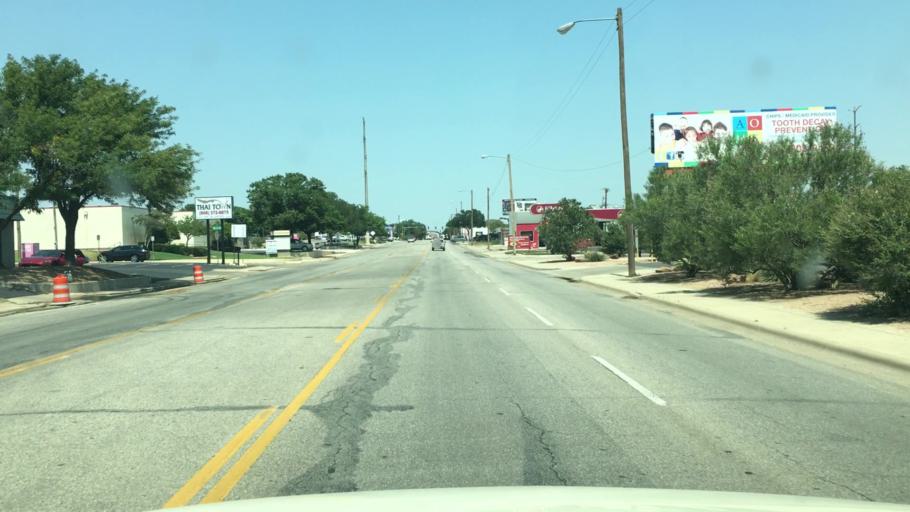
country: US
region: Texas
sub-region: Potter County
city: Amarillo
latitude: 35.1968
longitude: -101.8168
